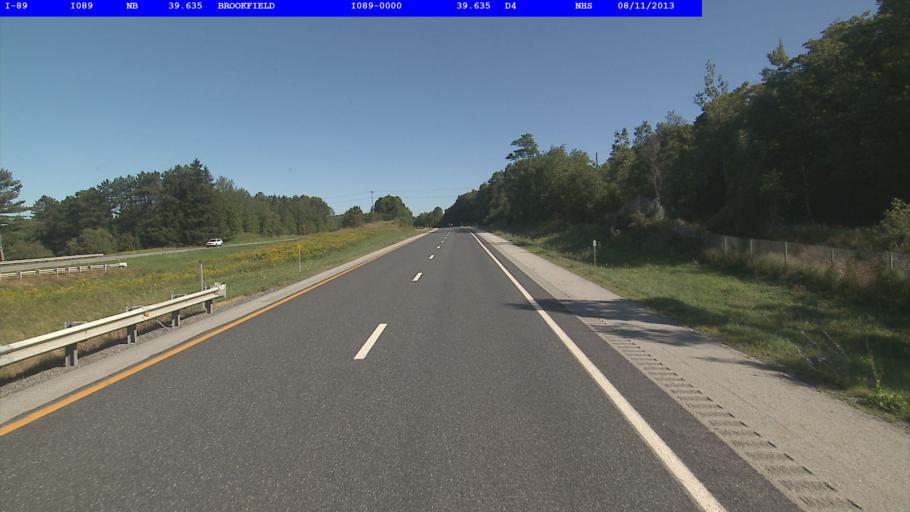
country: US
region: Vermont
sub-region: Orange County
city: Williamstown
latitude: 44.0685
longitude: -72.6074
